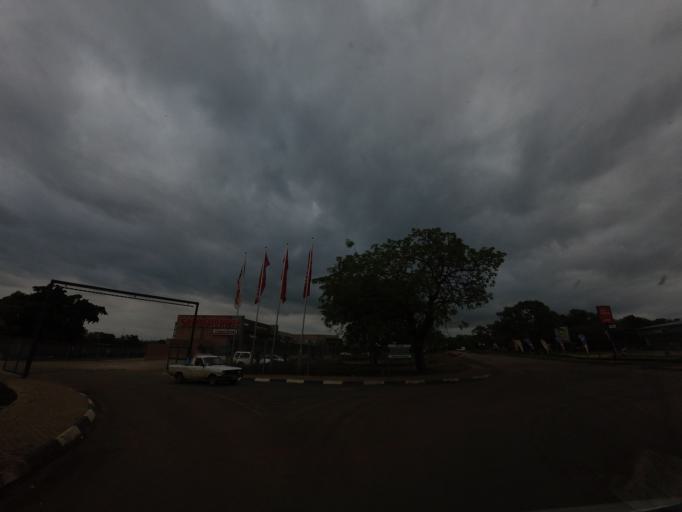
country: ZA
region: Mpumalanga
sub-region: Ehlanzeni District
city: Komatipoort
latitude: -25.4386
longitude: 31.9606
